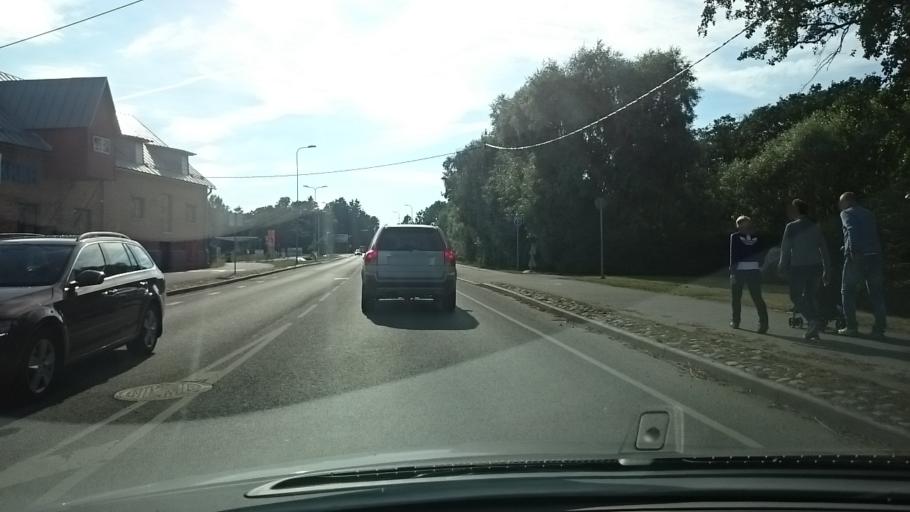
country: EE
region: Laeaene
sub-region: Ridala Parish
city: Uuemoisa
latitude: 58.9373
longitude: 23.5686
